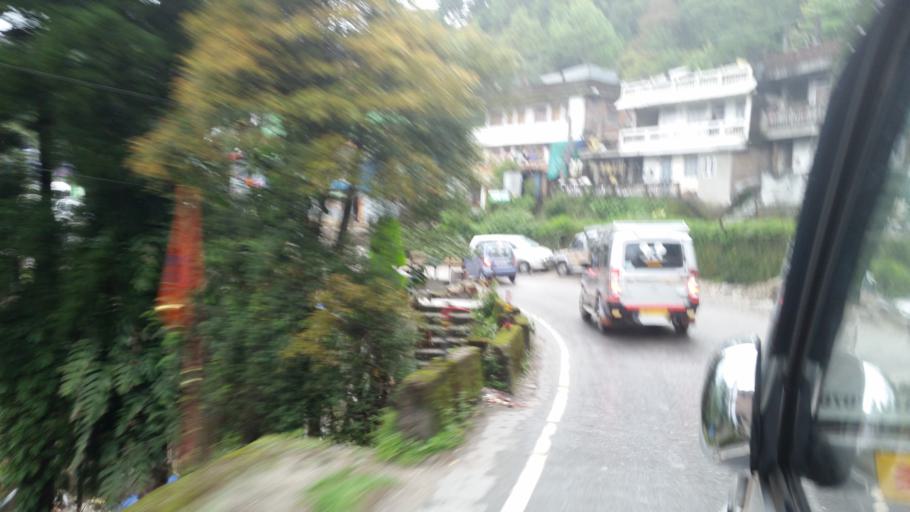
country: IN
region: West Bengal
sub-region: Darjiling
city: Darjiling
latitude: 27.0137
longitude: 88.2507
